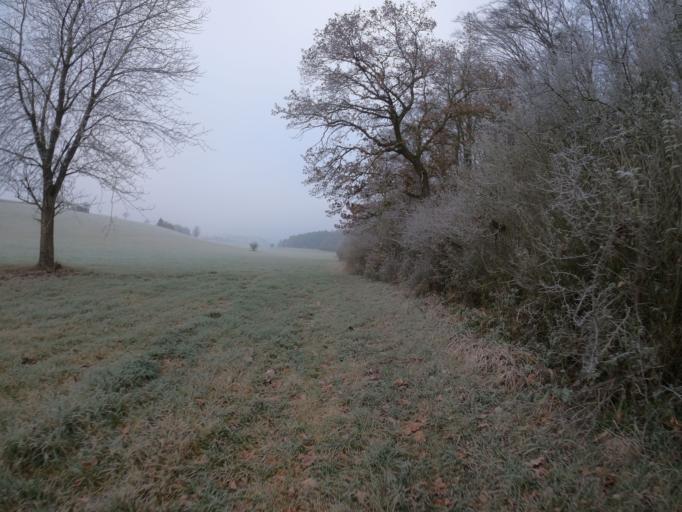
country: DE
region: Baden-Wuerttemberg
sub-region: Tuebingen Region
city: Westerstetten
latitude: 48.4964
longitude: 9.9597
